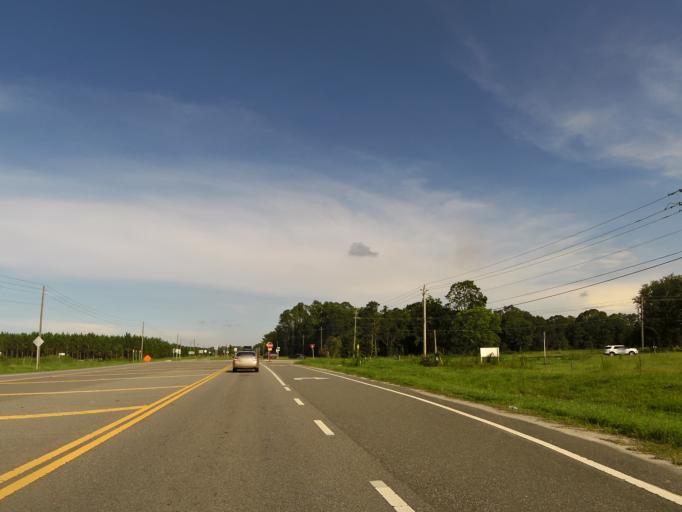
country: US
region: Florida
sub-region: Clay County
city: Green Cove Springs
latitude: 29.9763
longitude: -81.5127
